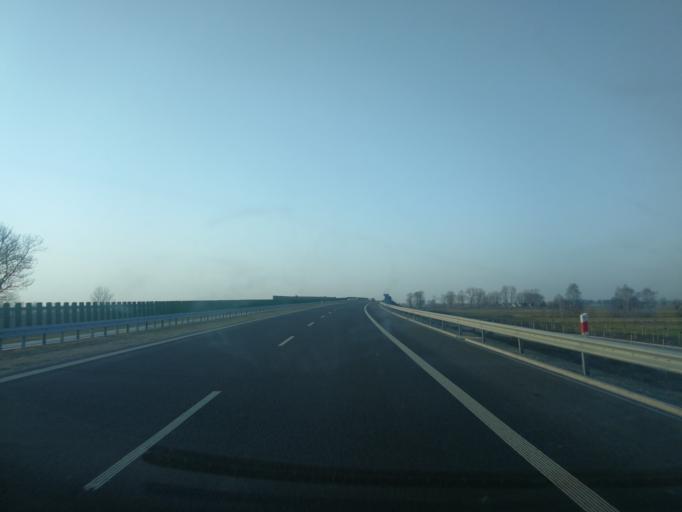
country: PL
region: Pomeranian Voivodeship
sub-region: Powiat nowodworski
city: Nowy Dwor Gdanski
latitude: 54.1784
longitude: 19.1849
